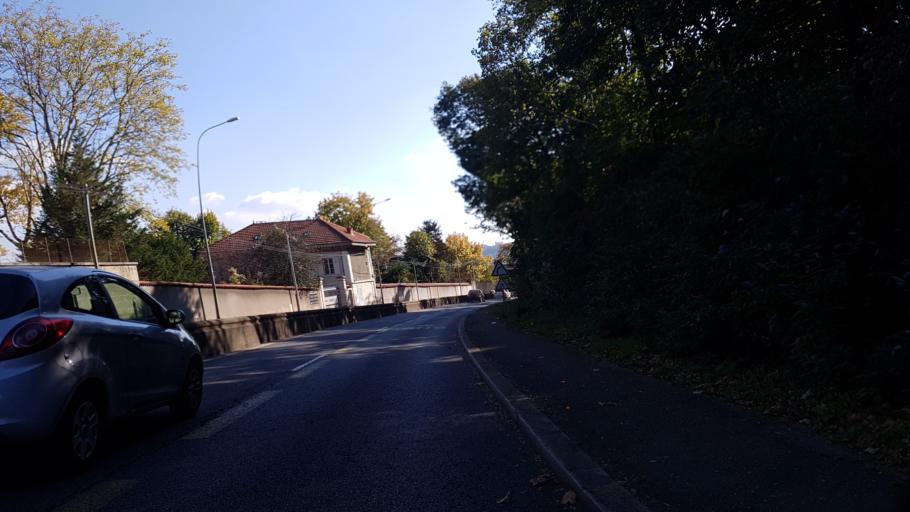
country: FR
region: Rhone-Alpes
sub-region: Departement du Rhone
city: Ecully
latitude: 45.7893
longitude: 4.8044
